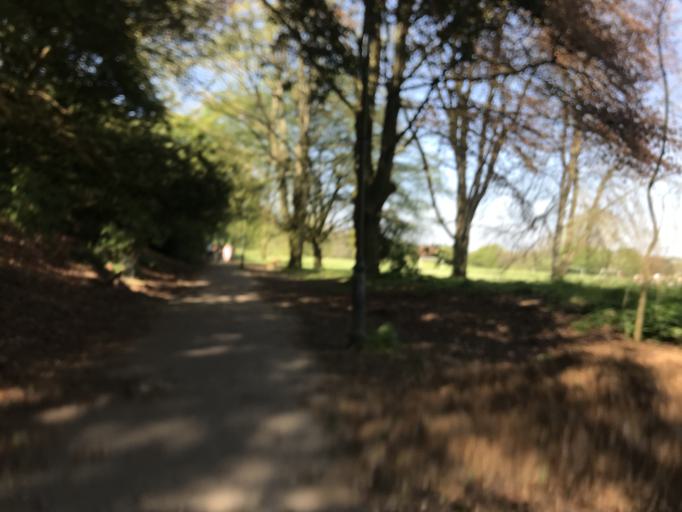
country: GB
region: England
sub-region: Devon
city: Barnstaple
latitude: 51.0681
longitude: -4.0531
